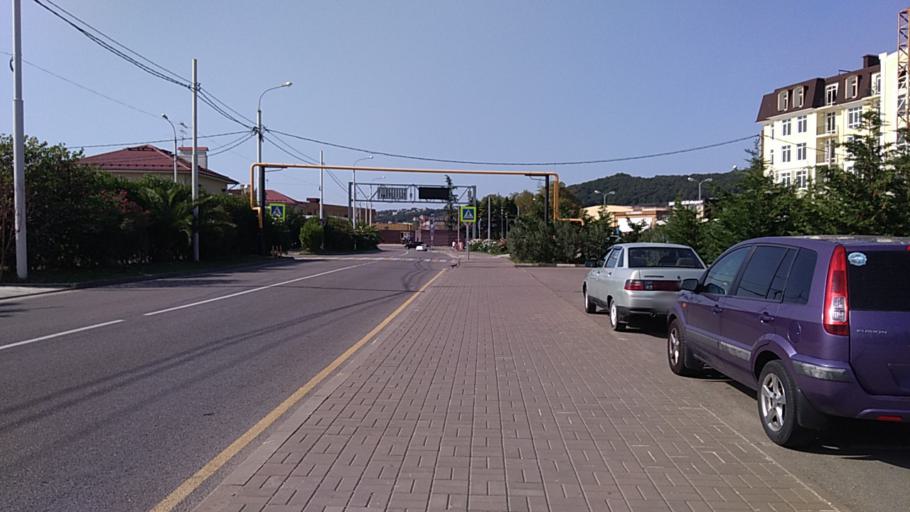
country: RU
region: Krasnodarskiy
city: Vysokoye
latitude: 43.3972
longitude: 39.9959
